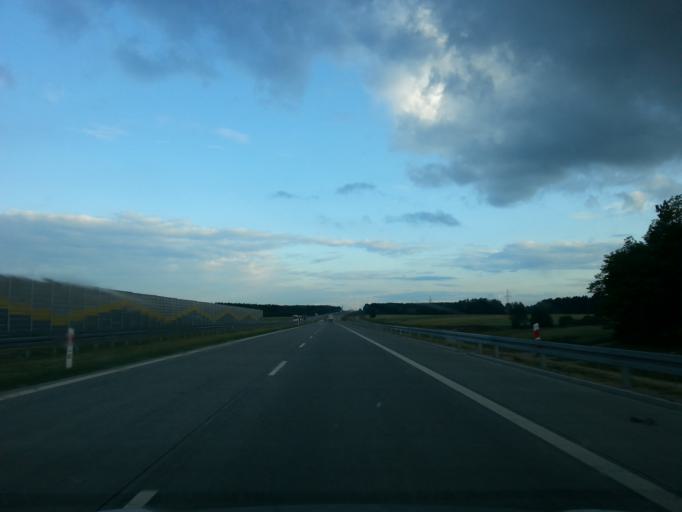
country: PL
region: Lodz Voivodeship
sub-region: Powiat sieradzki
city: Brzeznio
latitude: 51.5199
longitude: 18.6943
